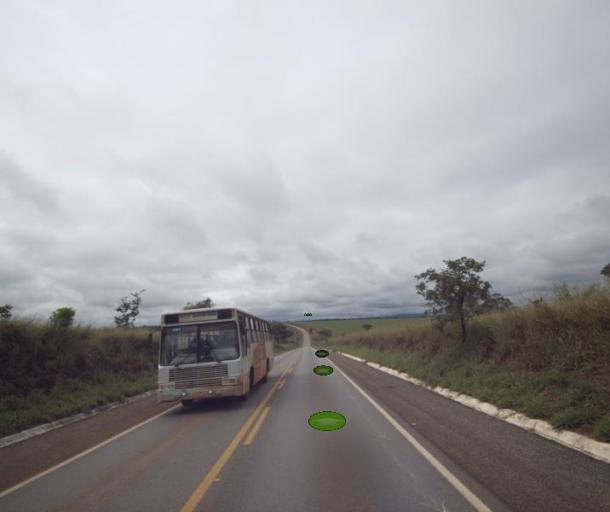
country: BR
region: Goias
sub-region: Uruacu
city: Uruacu
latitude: -14.6835
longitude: -49.1297
